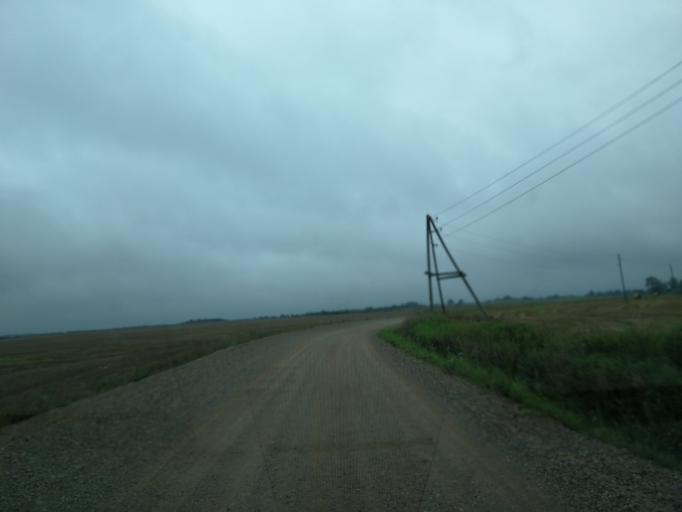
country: LV
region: Vilanu
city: Vilani
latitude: 56.3737
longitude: 27.0440
